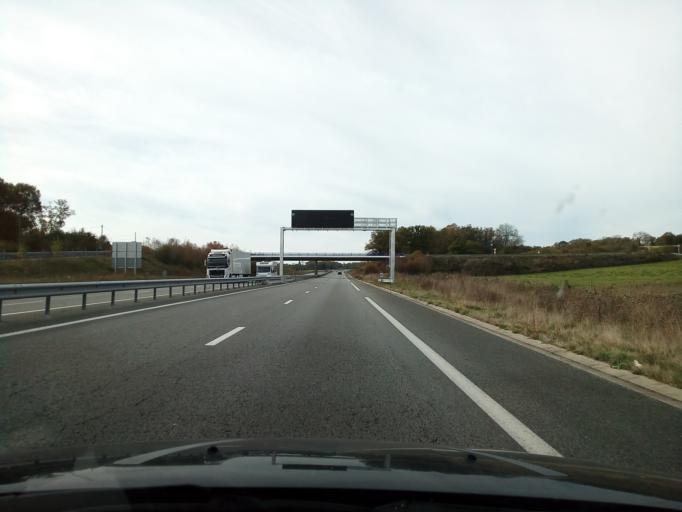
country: FR
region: Limousin
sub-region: Departement de la Creuse
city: Ajain
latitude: 46.2010
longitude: 2.1143
